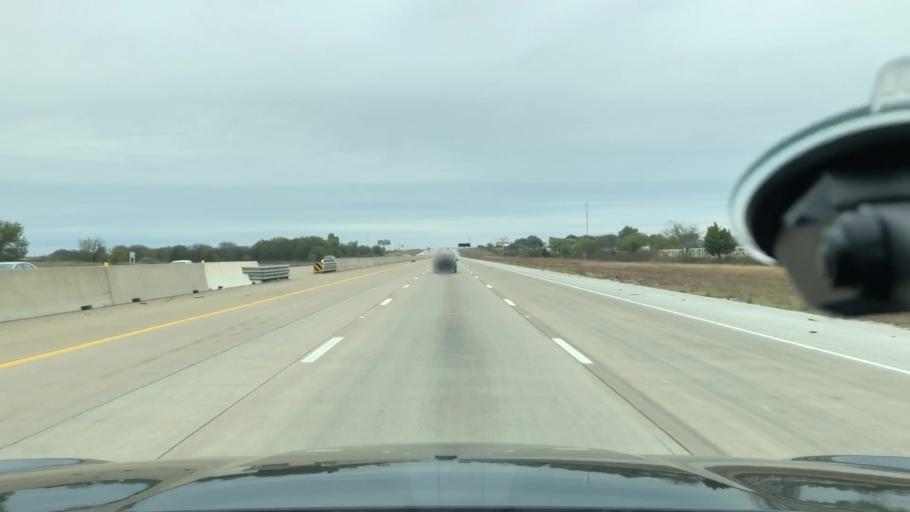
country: US
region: Texas
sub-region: Ellis County
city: Nash
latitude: 32.3074
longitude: -96.8631
